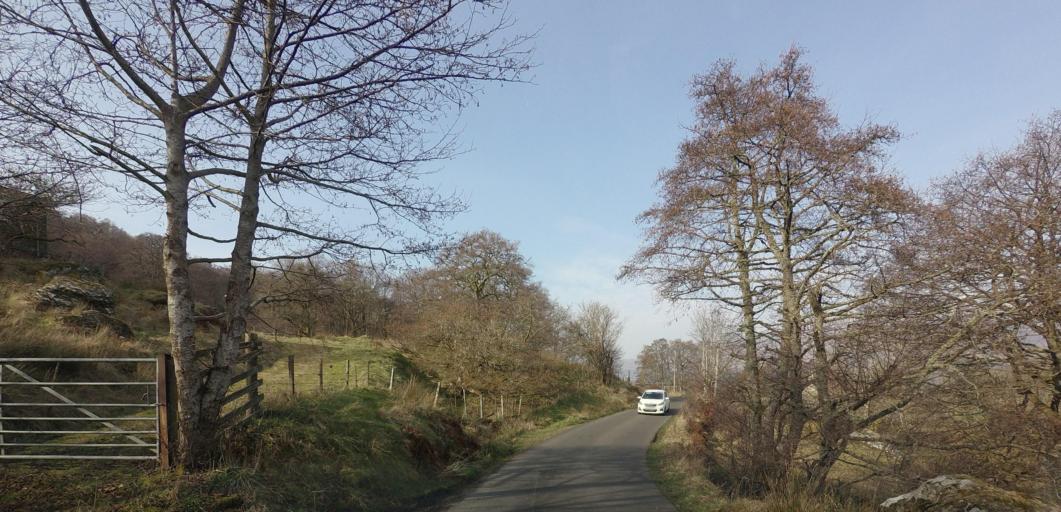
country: GB
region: Scotland
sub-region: Stirling
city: Callander
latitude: 56.4859
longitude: -4.2194
